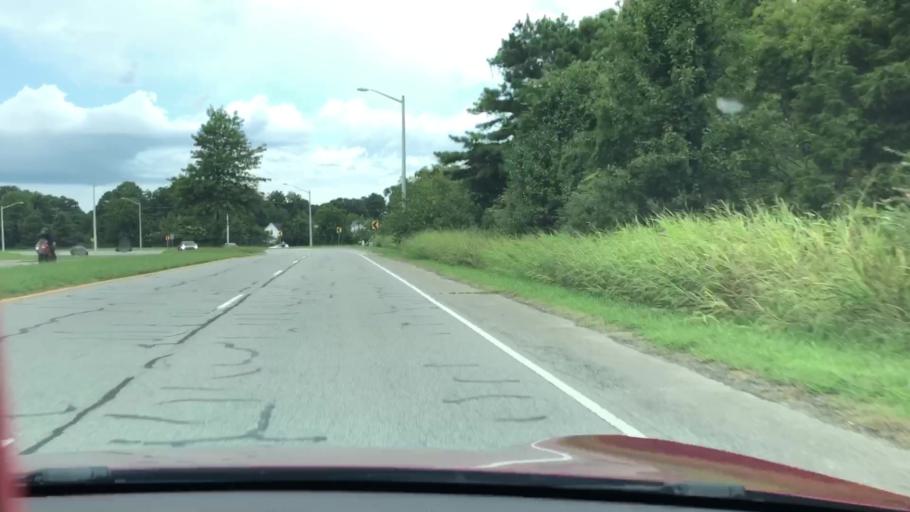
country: US
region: Virginia
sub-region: City of Virginia Beach
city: Virginia Beach
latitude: 36.8364
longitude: -76.0129
